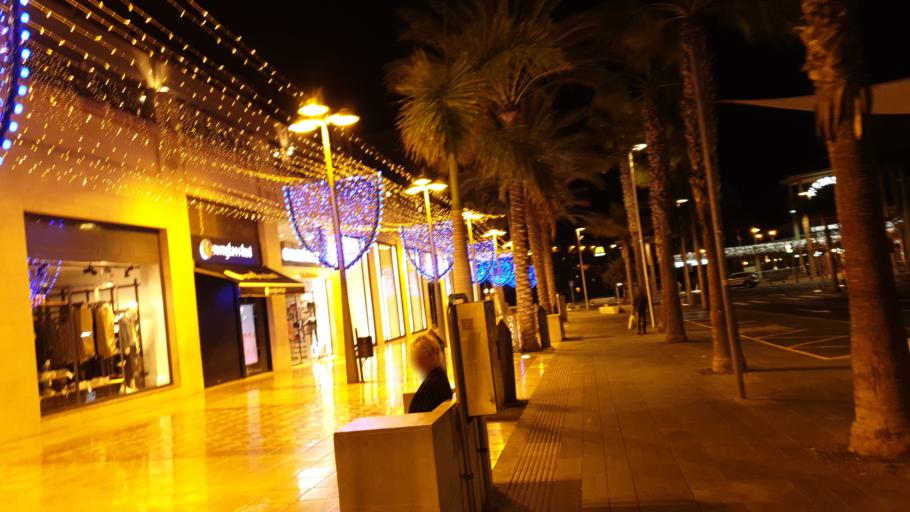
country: ES
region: Canary Islands
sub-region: Provincia de Santa Cruz de Tenerife
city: Playa de las Americas
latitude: 28.0542
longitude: -16.7277
